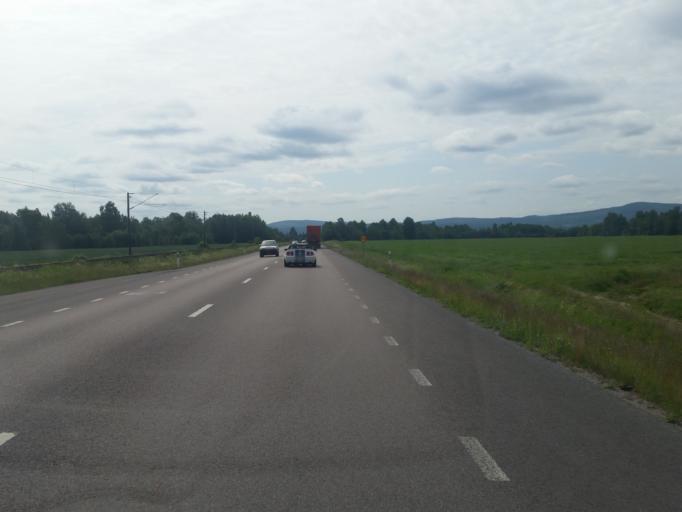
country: SE
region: Dalarna
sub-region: Gagnefs Kommun
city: Djuras
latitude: 60.5745
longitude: 15.1234
